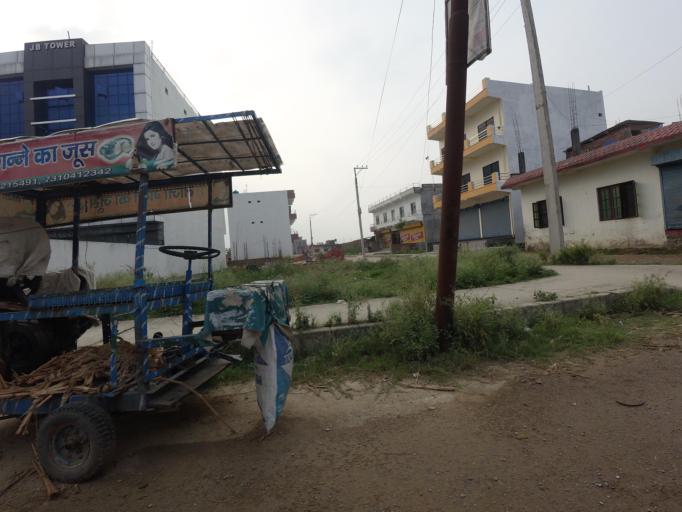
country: NP
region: Western Region
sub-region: Lumbini Zone
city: Bhairahawa
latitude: 27.5188
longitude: 83.4420
